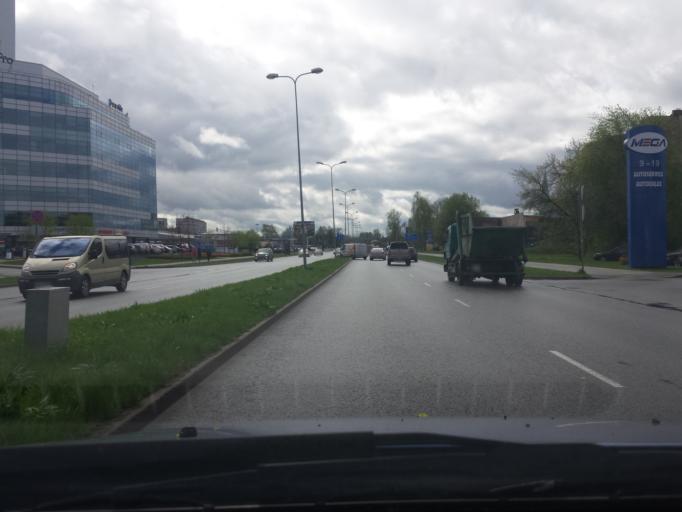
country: LV
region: Riga
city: Riga
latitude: 56.9529
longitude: 24.1874
